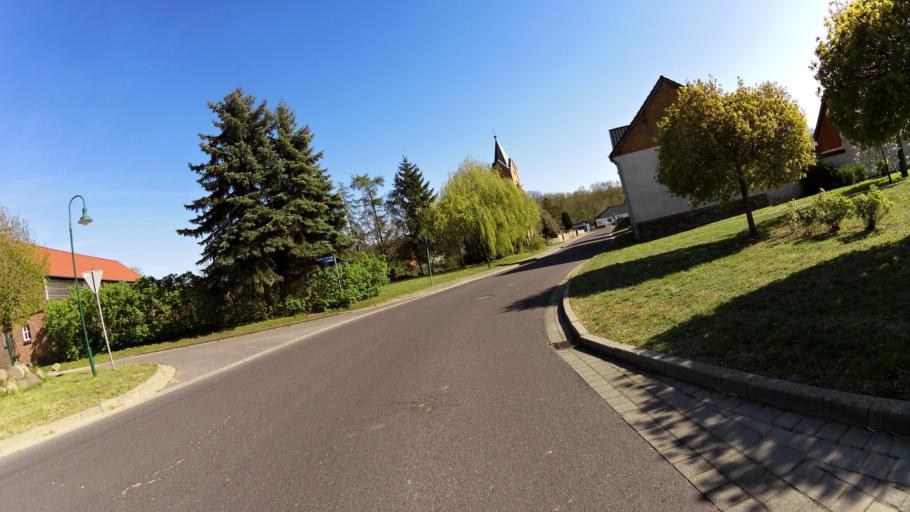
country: DE
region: Saxony-Anhalt
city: Uchtspringe
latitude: 52.5869
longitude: 11.6655
